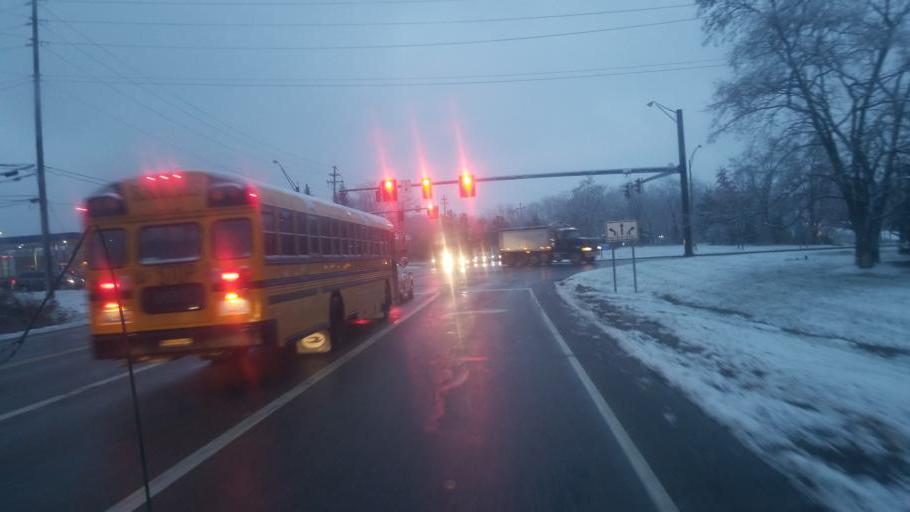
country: US
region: Ohio
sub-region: Geauga County
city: Bainbridge
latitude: 41.3889
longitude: -81.3400
